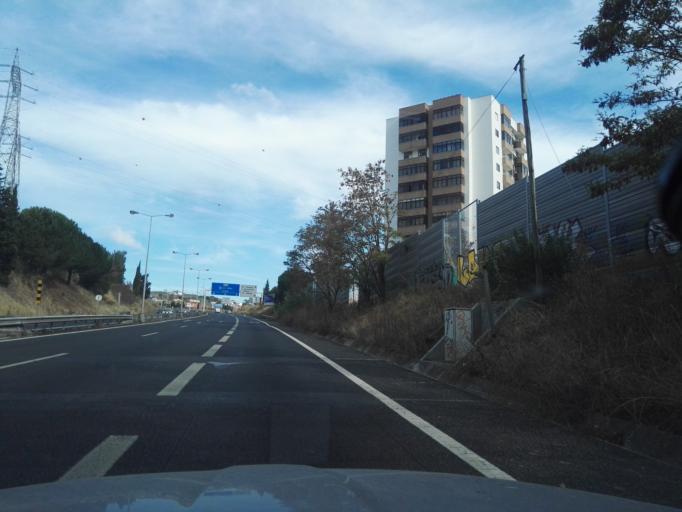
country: PT
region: Lisbon
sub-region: Odivelas
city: Povoa de Santo Adriao
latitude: 38.7981
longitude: -9.1746
